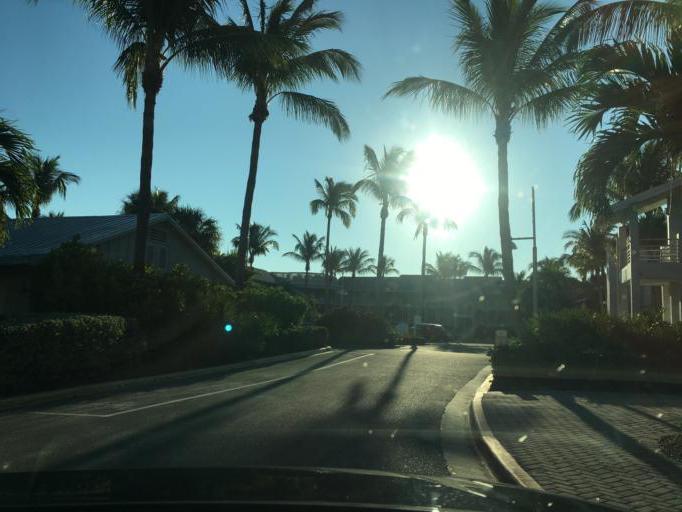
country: US
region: Florida
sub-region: Lee County
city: Pine Island Center
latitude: 26.5493
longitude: -82.1967
